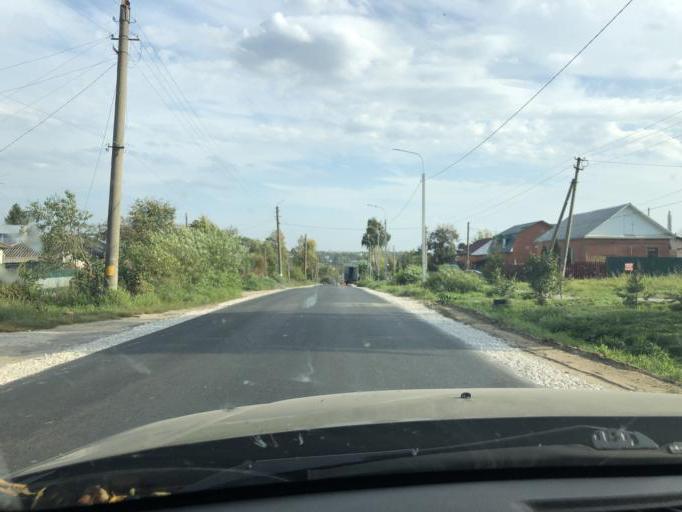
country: RU
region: Tula
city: Leninskiy
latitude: 54.2958
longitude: 37.4607
